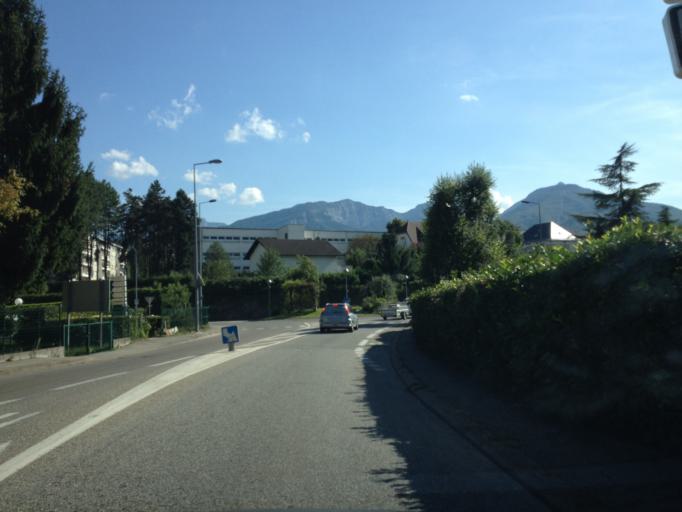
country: FR
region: Rhone-Alpes
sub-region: Departement de la Savoie
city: Cognin
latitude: 45.5643
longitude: 5.9034
